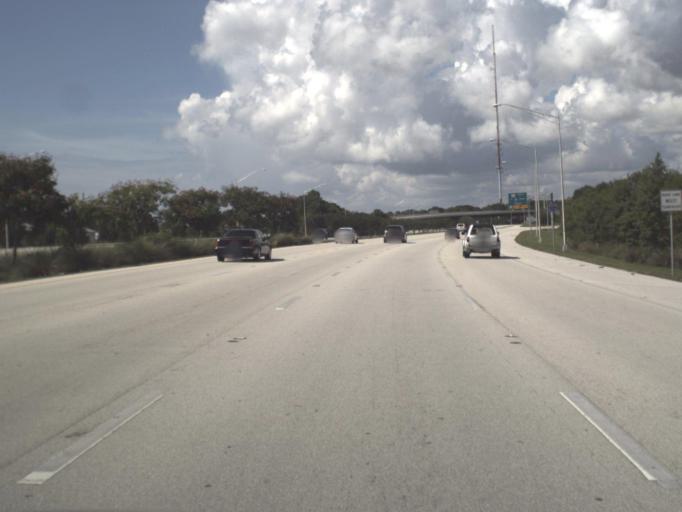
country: US
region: Florida
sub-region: Sarasota County
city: Laurel
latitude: 27.1444
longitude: -82.4615
